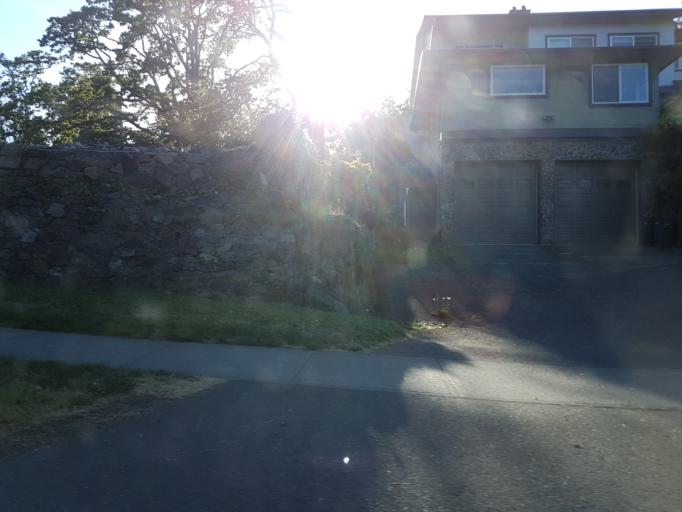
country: CA
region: British Columbia
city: Oak Bay
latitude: 48.4639
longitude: -123.3363
